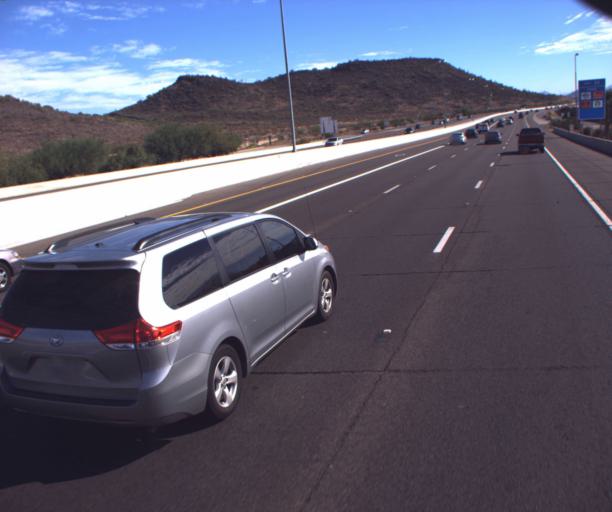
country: US
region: Arizona
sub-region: Maricopa County
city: Peoria
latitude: 33.6685
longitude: -112.1671
